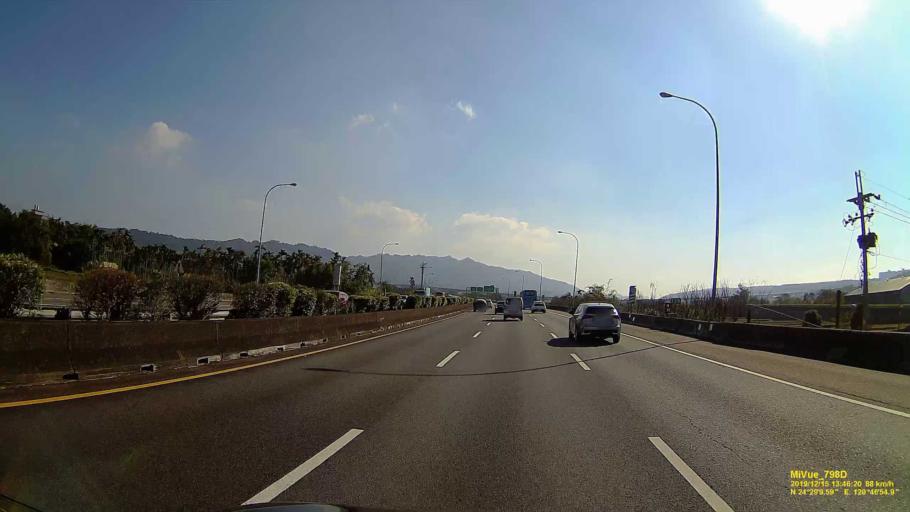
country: TW
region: Taiwan
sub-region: Miaoli
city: Miaoli
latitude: 24.4855
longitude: 120.7820
